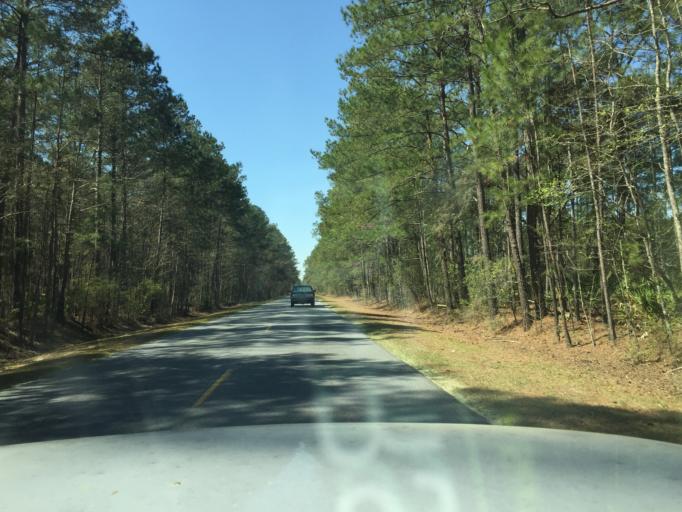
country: US
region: Georgia
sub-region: Chatham County
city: Bloomingdale
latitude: 32.0955
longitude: -81.3244
